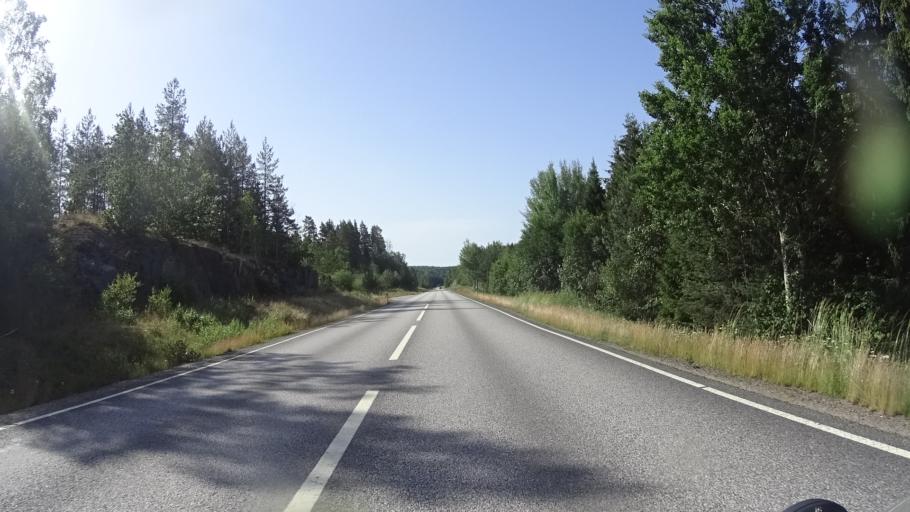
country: SE
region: Kalmar
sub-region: Vasterviks Kommun
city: Overum
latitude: 58.0697
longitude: 16.2002
